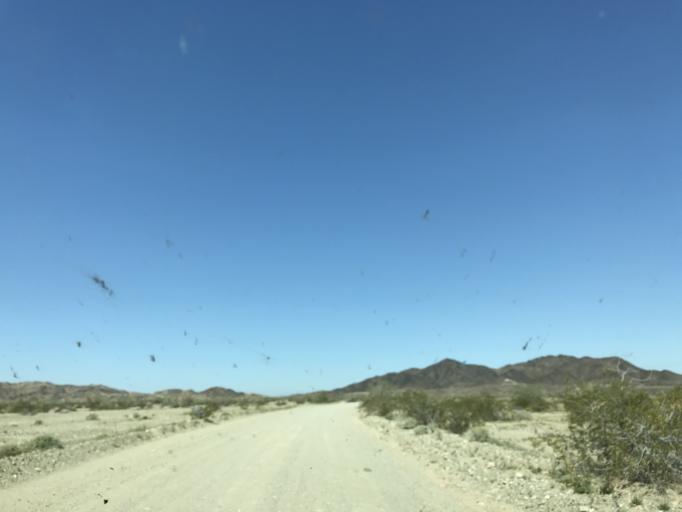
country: US
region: California
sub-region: Riverside County
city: Mesa Verde
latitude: 33.4913
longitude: -114.8050
